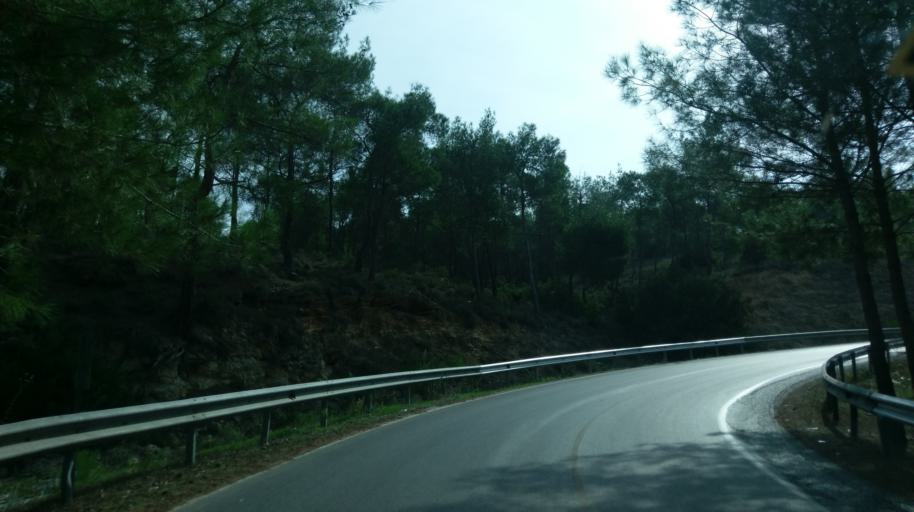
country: CY
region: Lefkosia
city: Morfou
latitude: 35.2707
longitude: 33.0443
